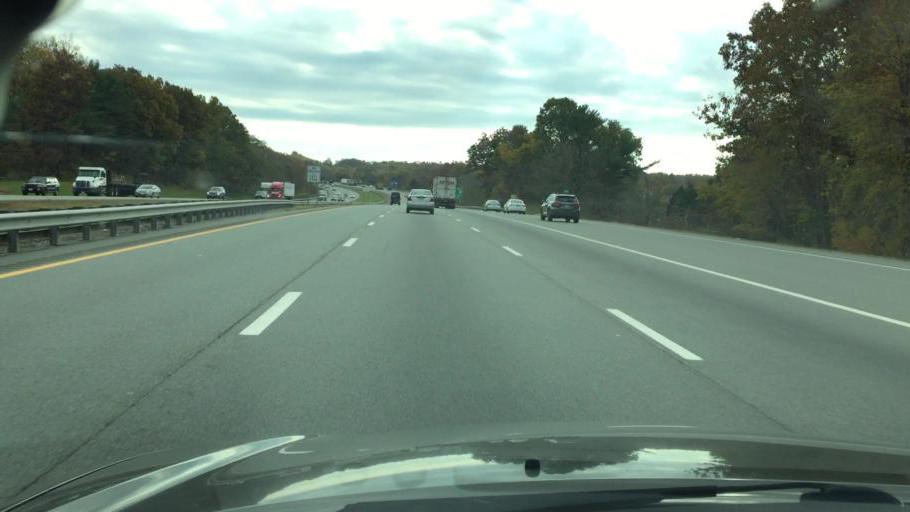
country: US
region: New Jersey
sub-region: Sussex County
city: Stanhope
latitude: 40.8996
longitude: -74.7194
